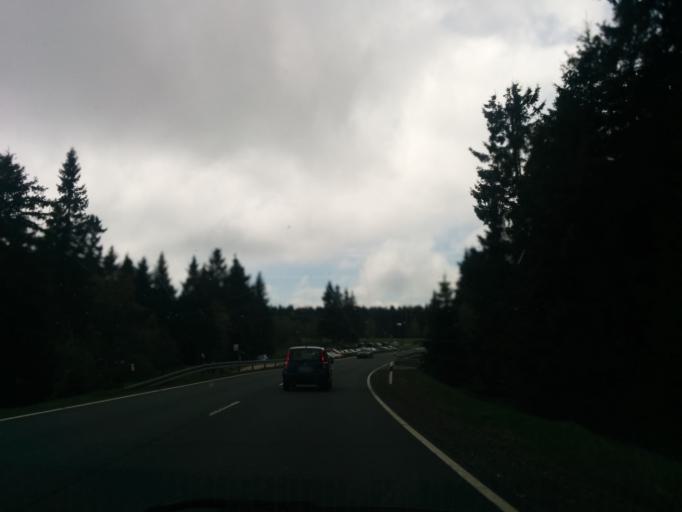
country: DE
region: Lower Saxony
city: Sankt Andreasberg
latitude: 51.7766
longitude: 10.5521
